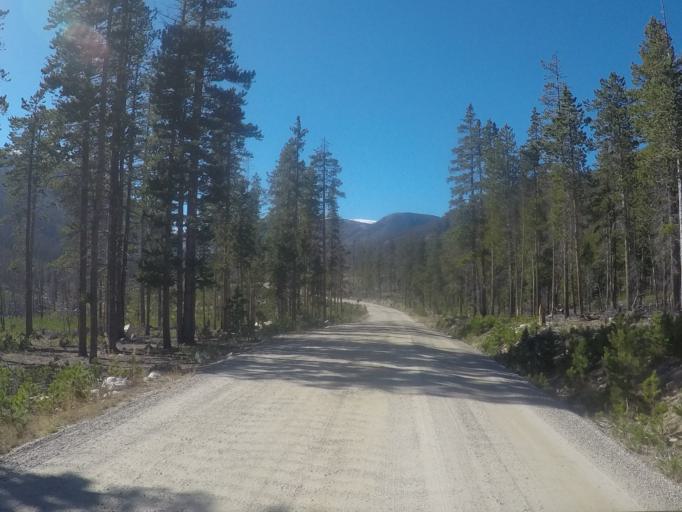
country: US
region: Montana
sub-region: Carbon County
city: Red Lodge
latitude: 45.1744
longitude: -109.4418
